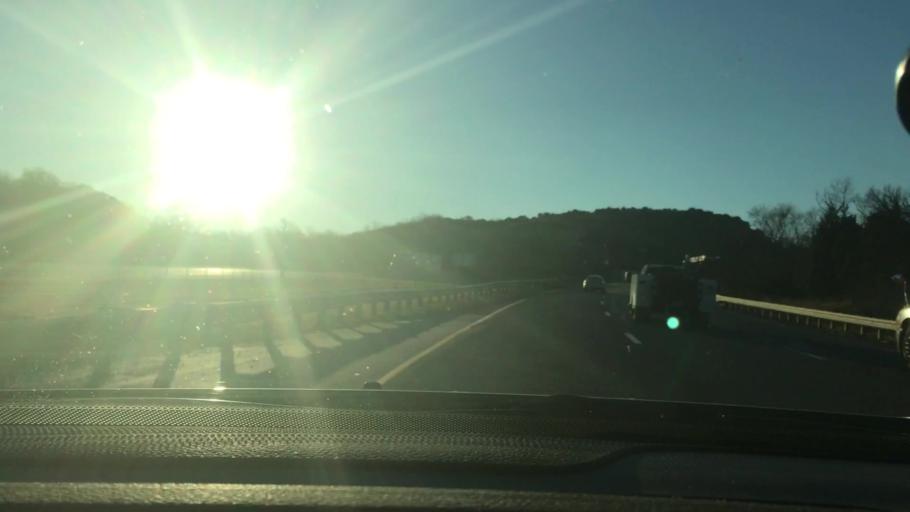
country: US
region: Oklahoma
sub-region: Murray County
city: Davis
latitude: 34.4453
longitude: -97.1301
